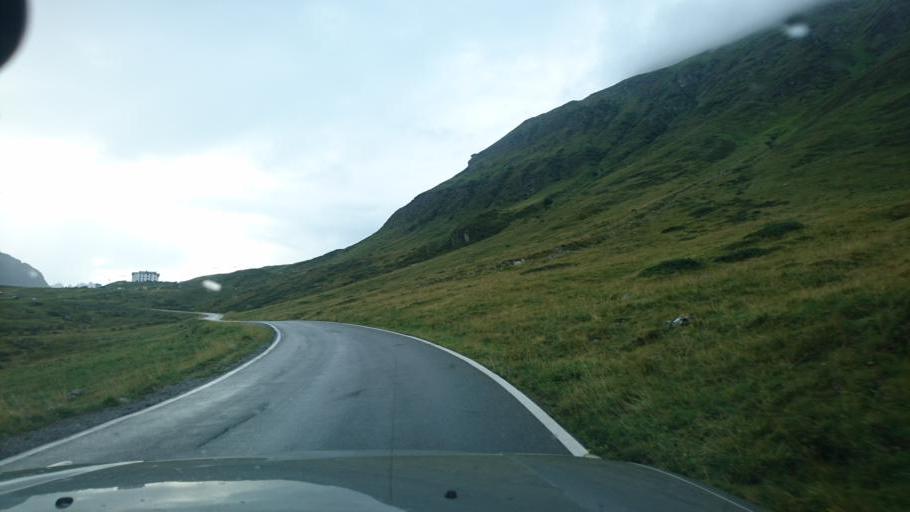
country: AT
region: Tyrol
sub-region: Politischer Bezirk Landeck
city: Galtur
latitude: 46.9198
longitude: 10.1049
